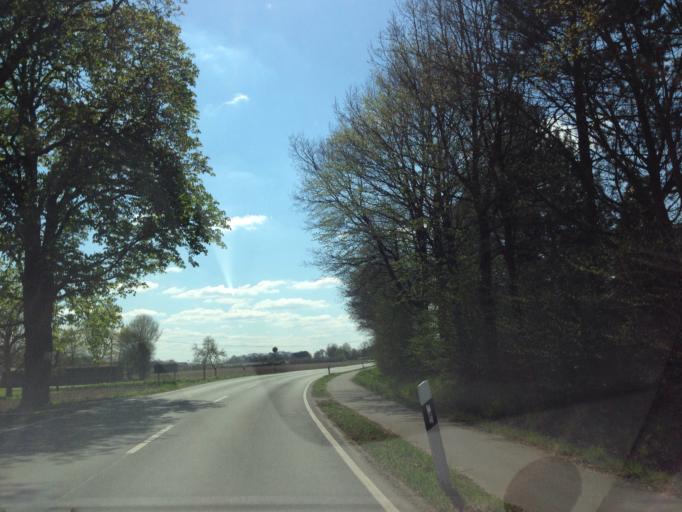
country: DE
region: North Rhine-Westphalia
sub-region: Regierungsbezirk Munster
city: Muenster
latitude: 51.9103
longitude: 7.5918
